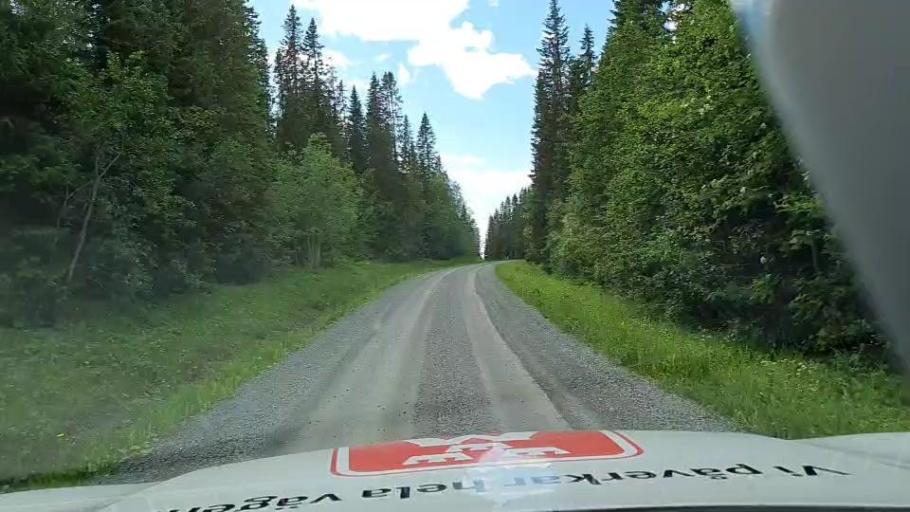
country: SE
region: Jaemtland
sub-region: Krokoms Kommun
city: Valla
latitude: 63.5666
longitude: 13.7926
